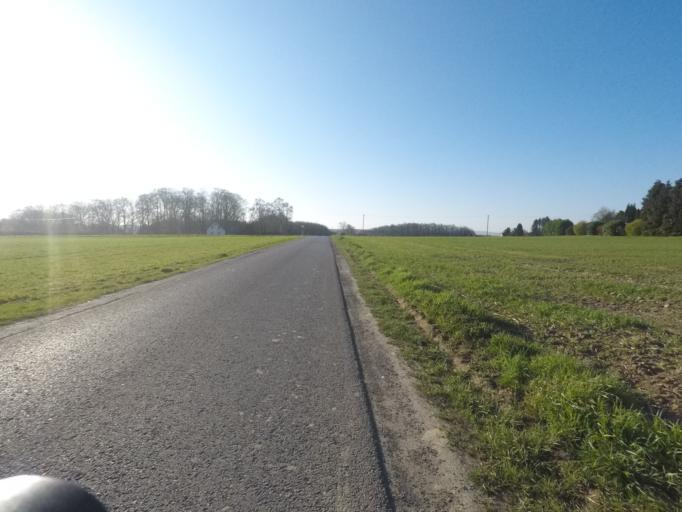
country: DE
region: North Rhine-Westphalia
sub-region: Regierungsbezirk Detmold
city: Herford
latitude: 52.0967
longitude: 8.6185
